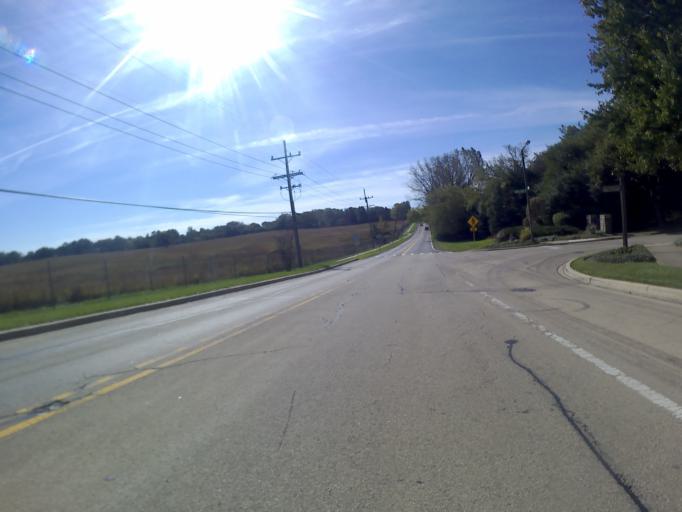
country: US
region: Illinois
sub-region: DuPage County
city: Lisle
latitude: 41.8147
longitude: -88.0940
